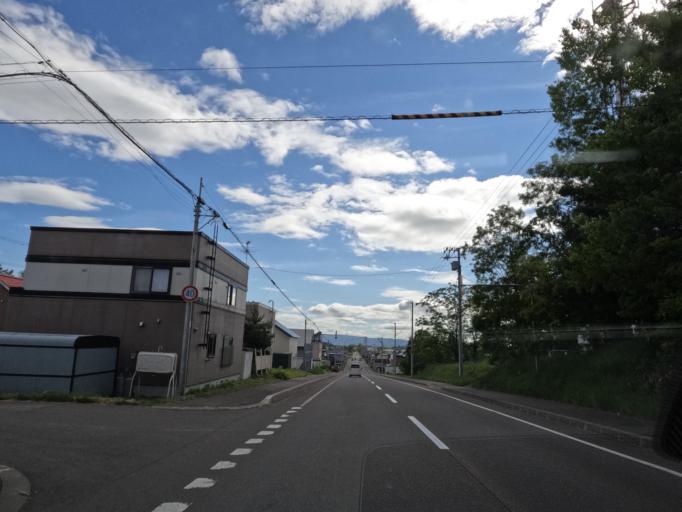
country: JP
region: Hokkaido
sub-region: Asahikawa-shi
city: Asahikawa
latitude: 43.8284
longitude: 142.5259
